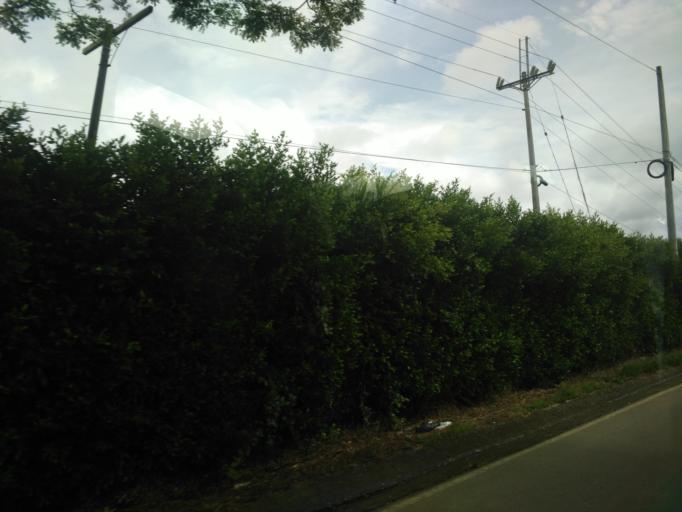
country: CO
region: Valle del Cauca
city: Caicedonia
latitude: 4.3358
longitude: -75.8621
